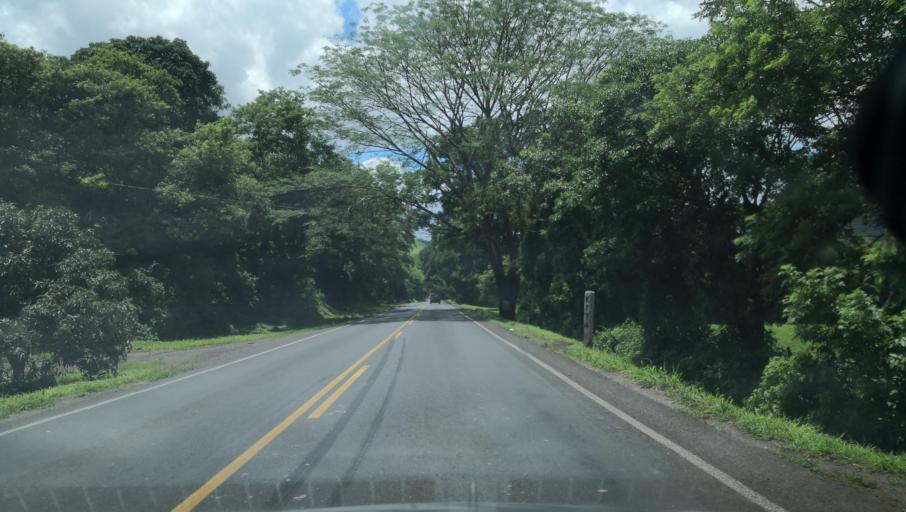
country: NI
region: Esteli
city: Condega
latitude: 13.2932
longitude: -86.3476
